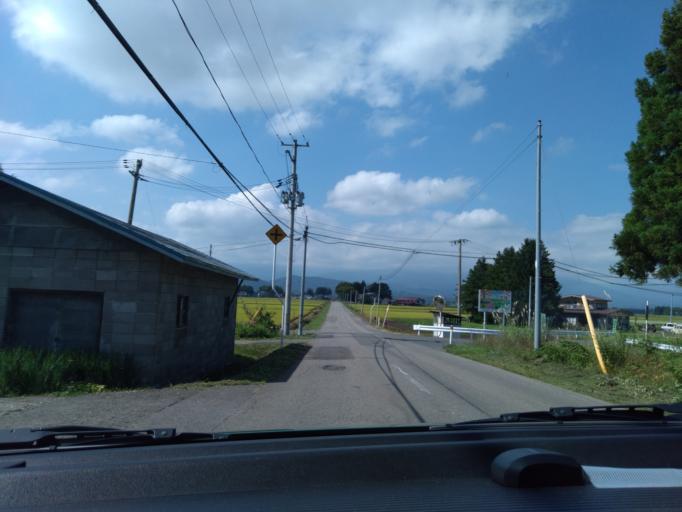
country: JP
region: Iwate
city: Shizukuishi
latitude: 39.6722
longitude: 140.9678
